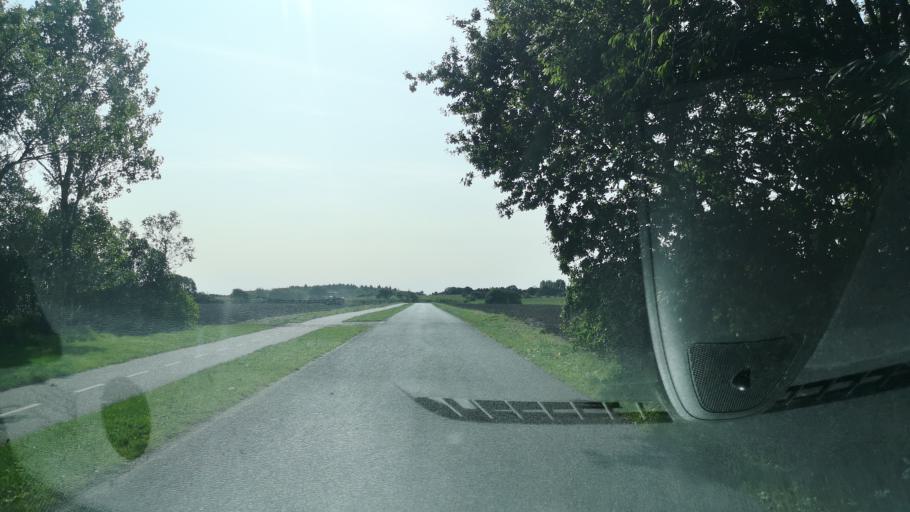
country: DK
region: Central Jutland
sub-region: Ringkobing-Skjern Kommune
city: Videbaek
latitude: 56.0770
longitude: 8.6141
